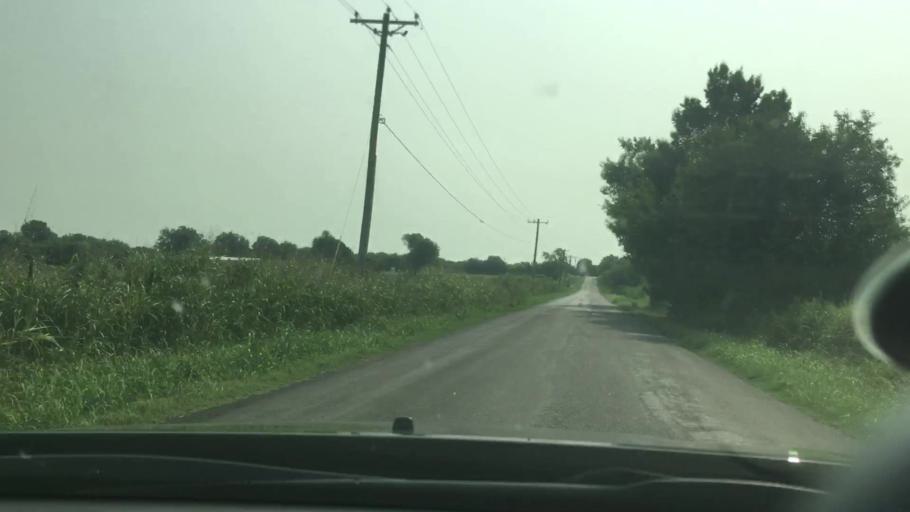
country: US
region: Oklahoma
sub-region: Garvin County
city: Lindsay
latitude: 34.8101
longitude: -97.6142
